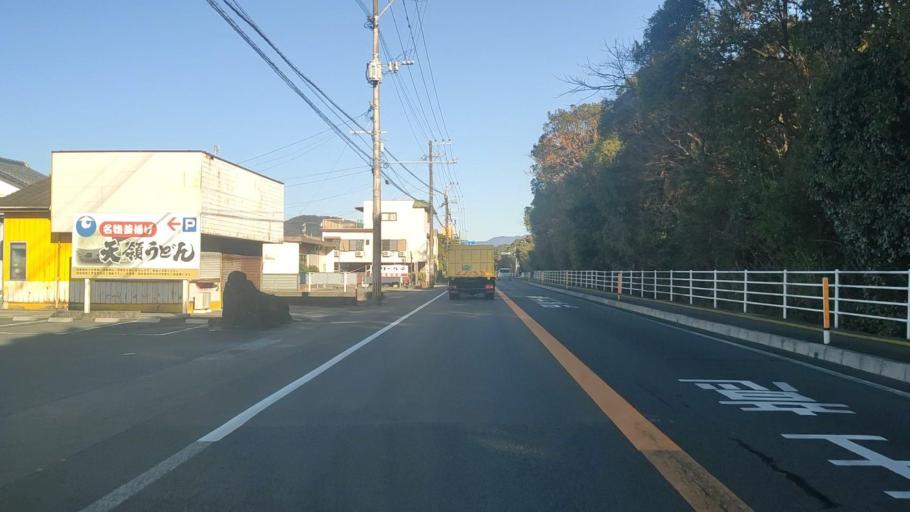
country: JP
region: Miyazaki
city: Nobeoka
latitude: 32.5270
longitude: 131.6823
